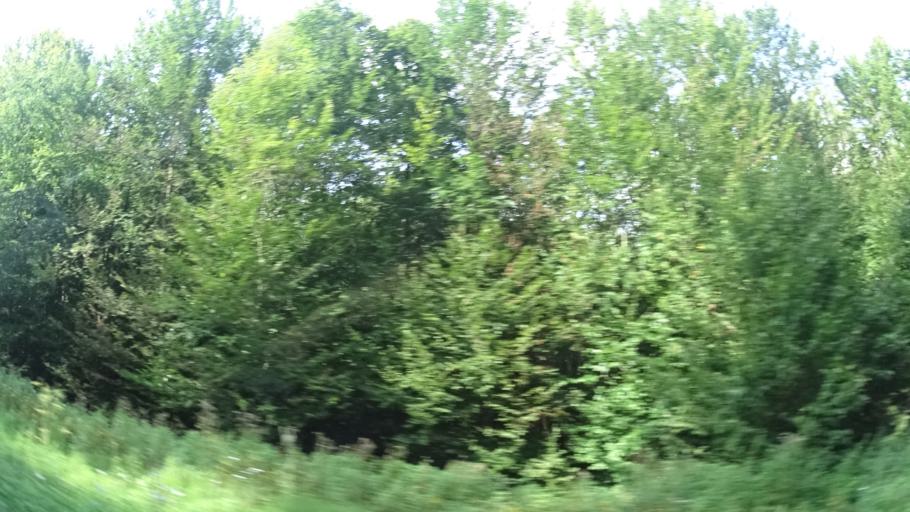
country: DE
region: Bavaria
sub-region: Regierungsbezirk Unterfranken
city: Arnstein
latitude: 49.9253
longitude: 9.9425
